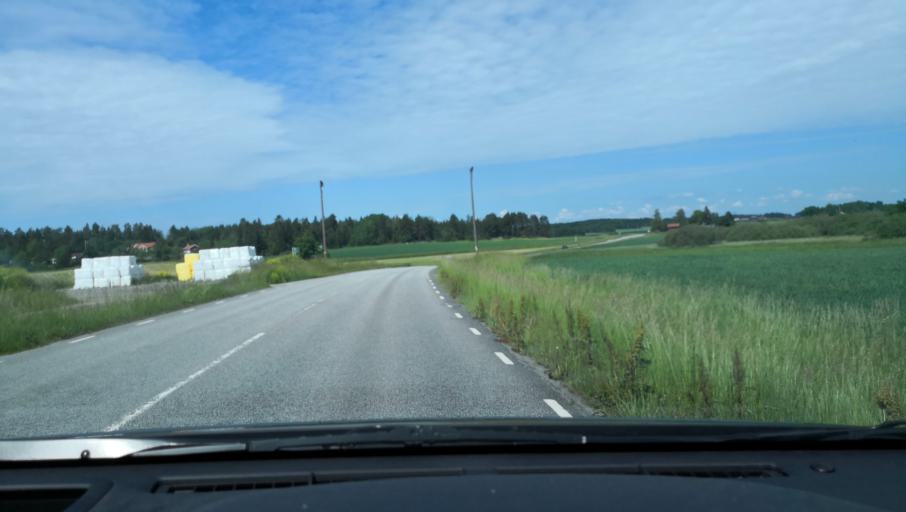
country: SE
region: Stockholm
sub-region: Sigtuna Kommun
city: Sigtuna
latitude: 59.6604
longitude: 17.6898
